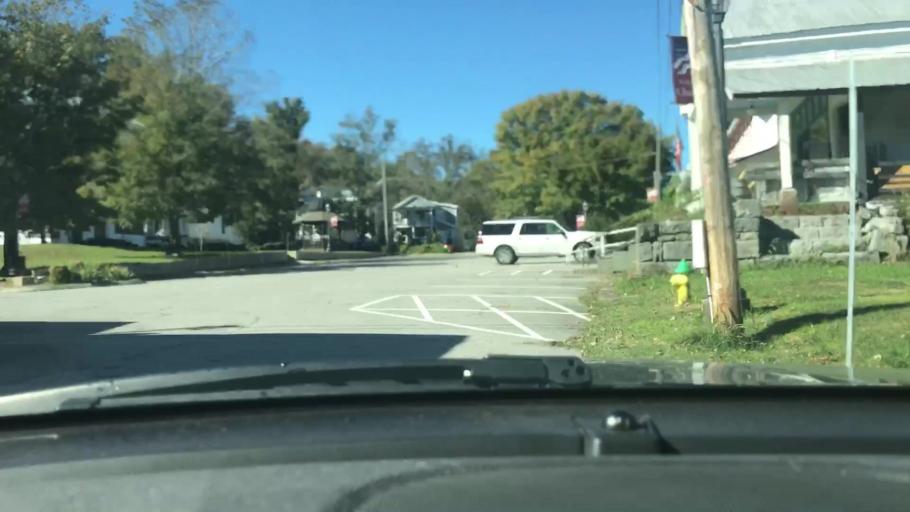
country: US
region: Tennessee
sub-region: Dickson County
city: Charlotte
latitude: 36.1781
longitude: -87.3388
